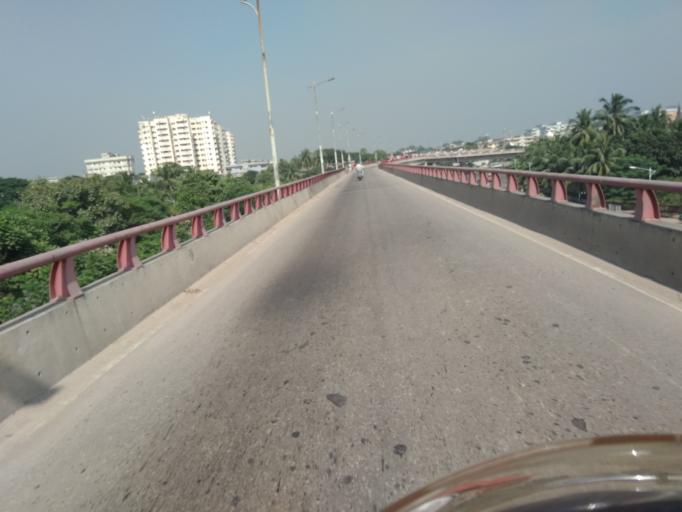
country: BD
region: Dhaka
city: Tungi
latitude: 23.8139
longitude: 90.4040
